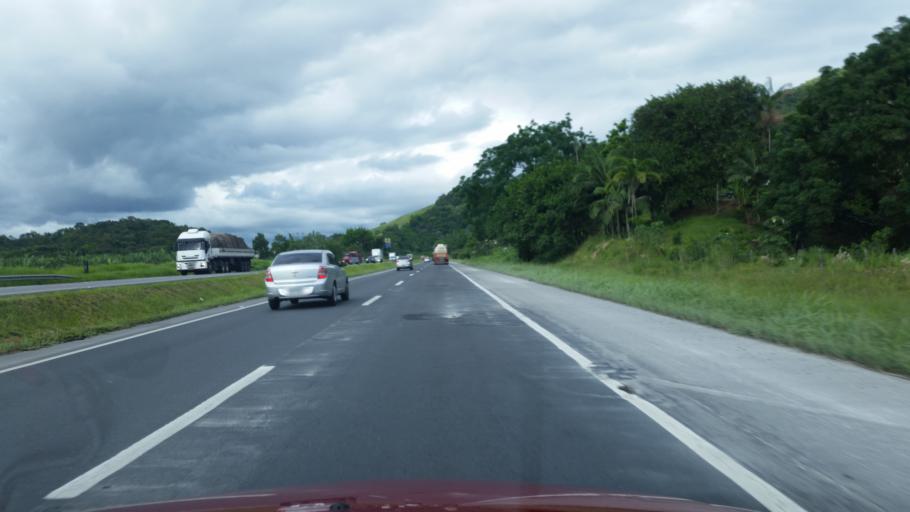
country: BR
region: Sao Paulo
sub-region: Miracatu
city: Miracatu
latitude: -24.3054
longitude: -47.4911
